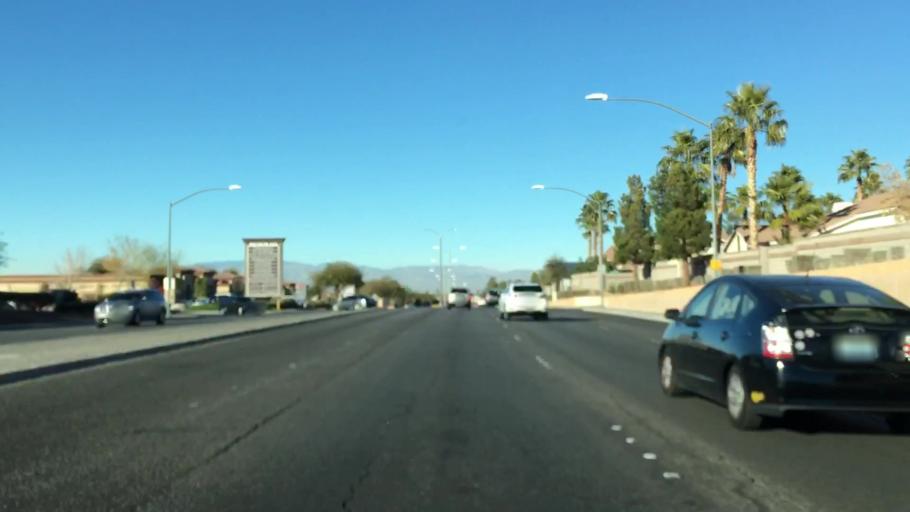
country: US
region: Nevada
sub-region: Clark County
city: Whitney
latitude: 36.0250
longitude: -115.1005
